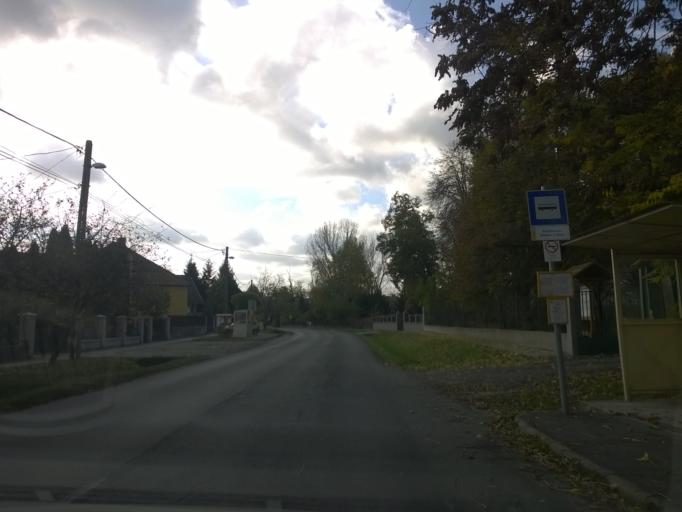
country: HU
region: Pest
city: Rackeve
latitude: 47.1354
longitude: 18.9477
